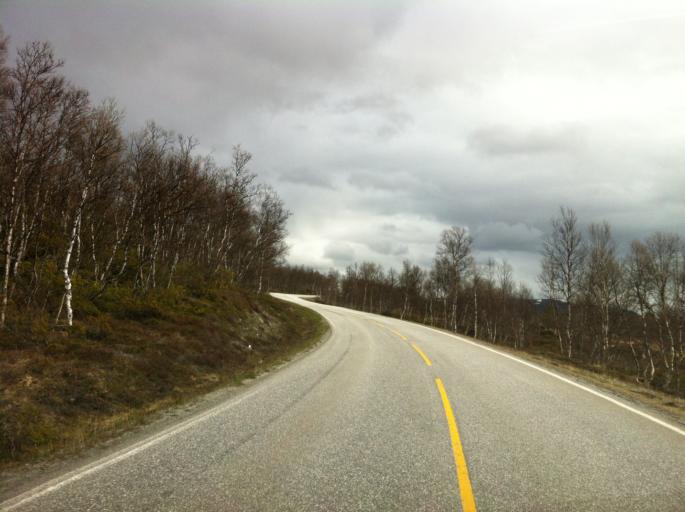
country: NO
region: Sor-Trondelag
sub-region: Roros
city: Roros
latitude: 62.5994
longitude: 11.5322
